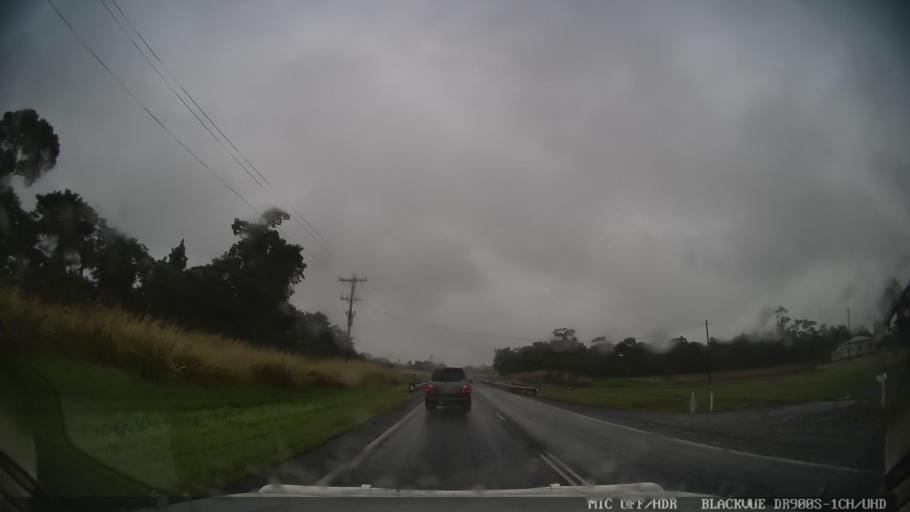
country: AU
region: Queensland
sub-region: Cassowary Coast
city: Innisfail
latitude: -17.6552
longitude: 146.0357
